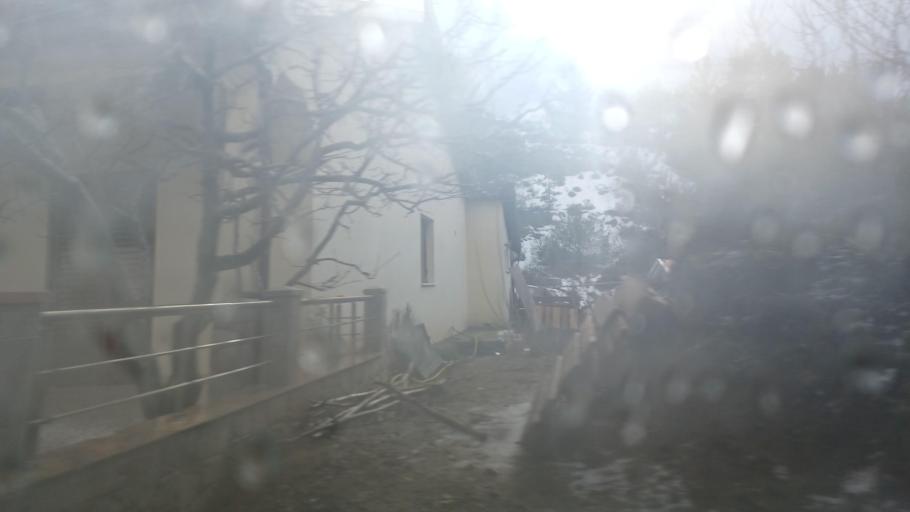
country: CY
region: Limassol
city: Kyperounta
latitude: 34.9437
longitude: 32.9595
